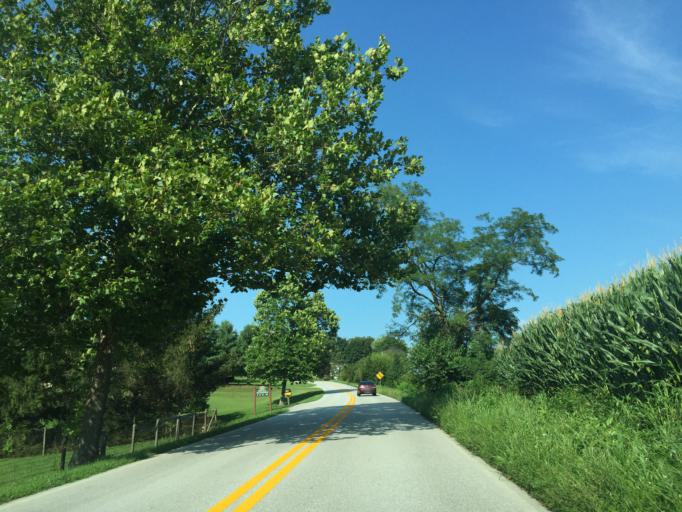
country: US
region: Maryland
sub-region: Carroll County
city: Manchester
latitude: 39.6323
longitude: -76.8869
